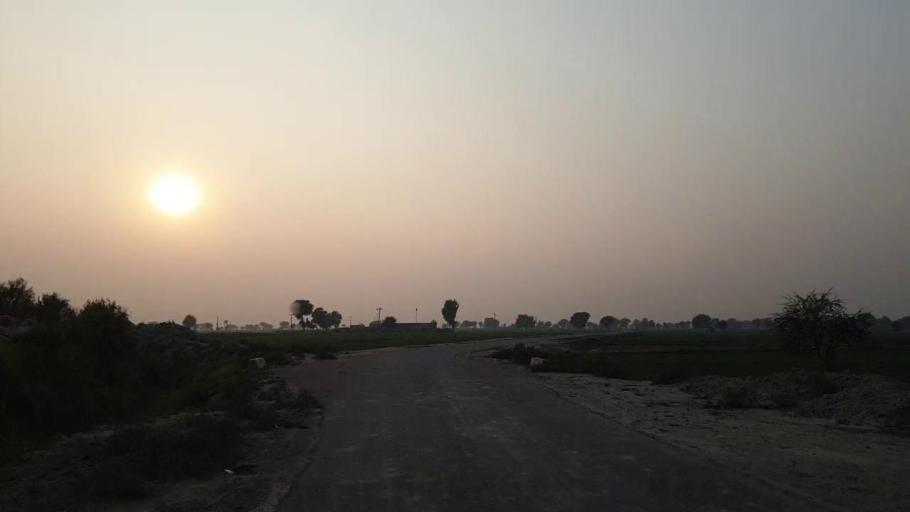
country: PK
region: Sindh
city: Bhan
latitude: 26.5306
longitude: 67.7000
